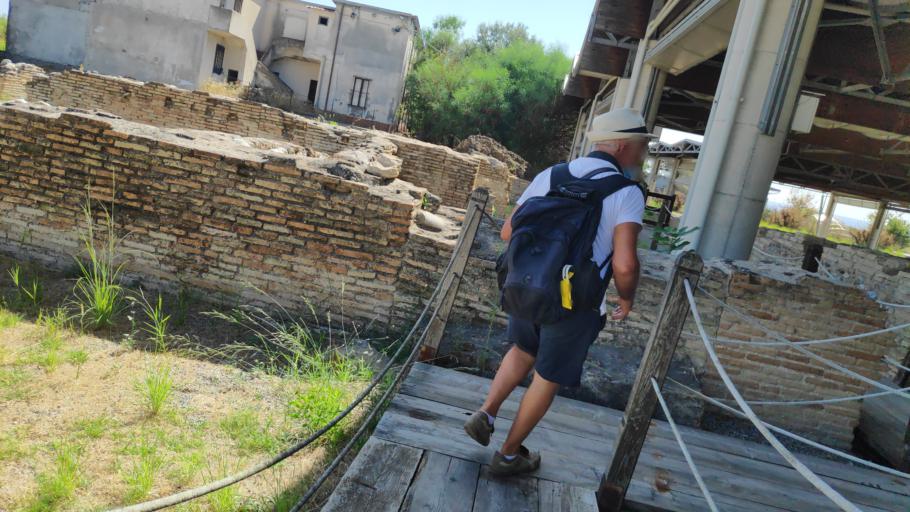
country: IT
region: Calabria
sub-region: Provincia di Reggio Calabria
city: Bianco
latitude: 38.1177
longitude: 16.1578
